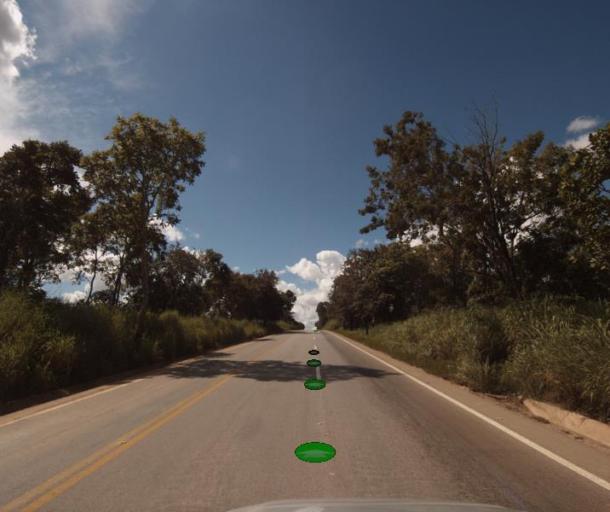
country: BR
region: Goias
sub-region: Porangatu
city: Porangatu
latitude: -13.4697
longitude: -49.1359
